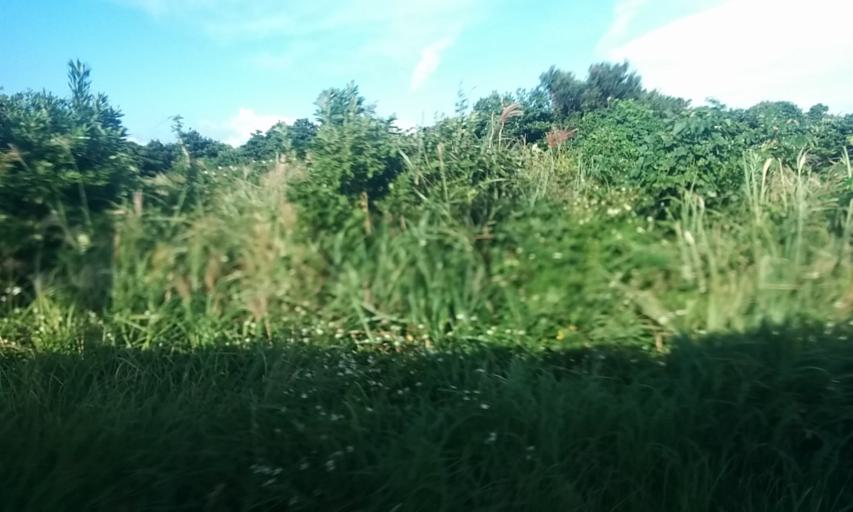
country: JP
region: Kagoshima
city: Nishinoomote
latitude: 30.3808
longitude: 130.6609
